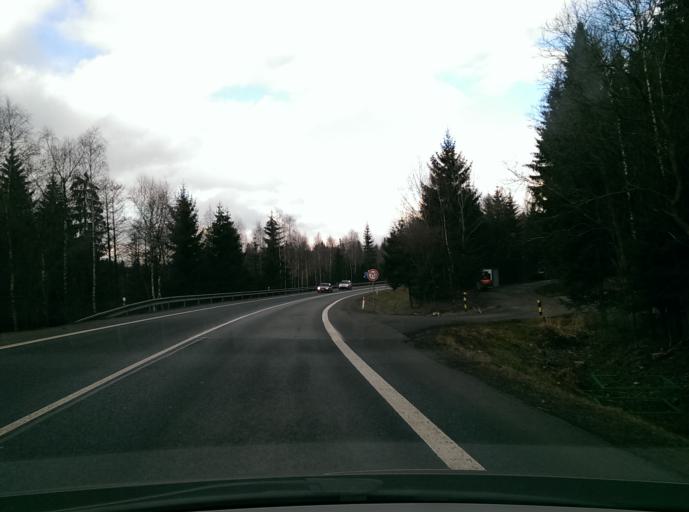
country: CZ
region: Liberecky
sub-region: Okres Jablonec nad Nisou
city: Jablonec nad Nisou
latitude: 50.7056
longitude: 15.1422
